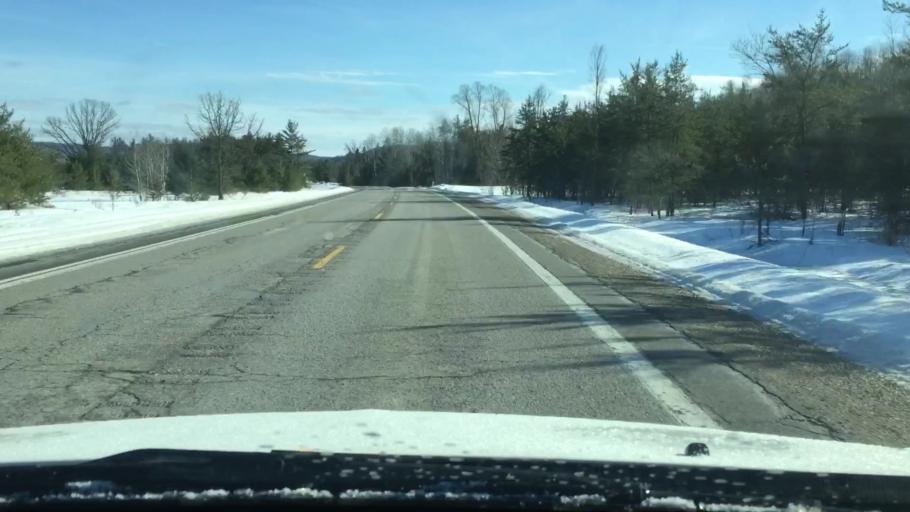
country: US
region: Michigan
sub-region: Charlevoix County
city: East Jordan
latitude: 45.1062
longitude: -85.1246
